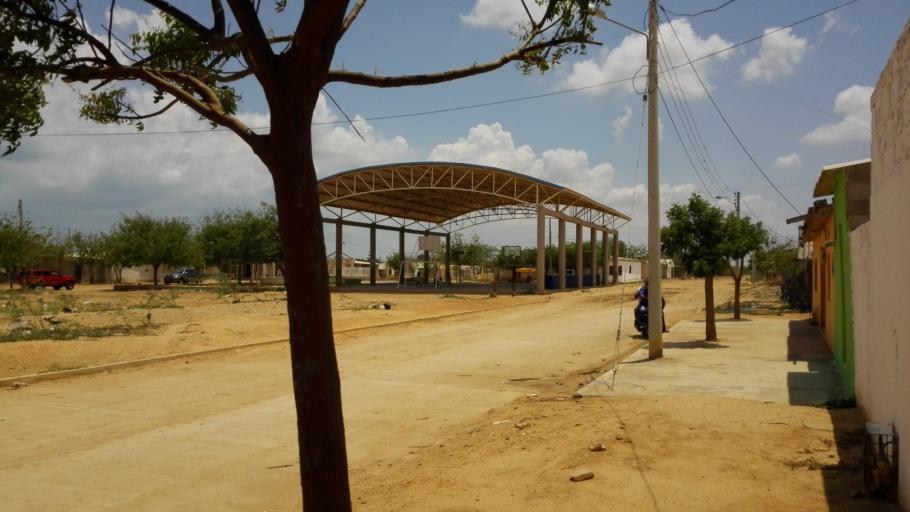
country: CO
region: La Guajira
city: Manaure
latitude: 11.7729
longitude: -72.4437
